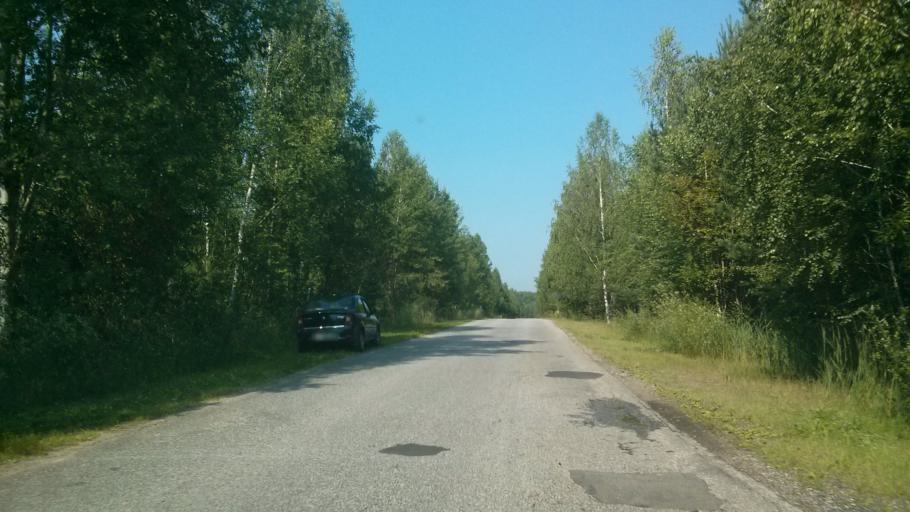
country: RU
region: Vladimir
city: Murom
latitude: 55.5057
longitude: 42.0040
